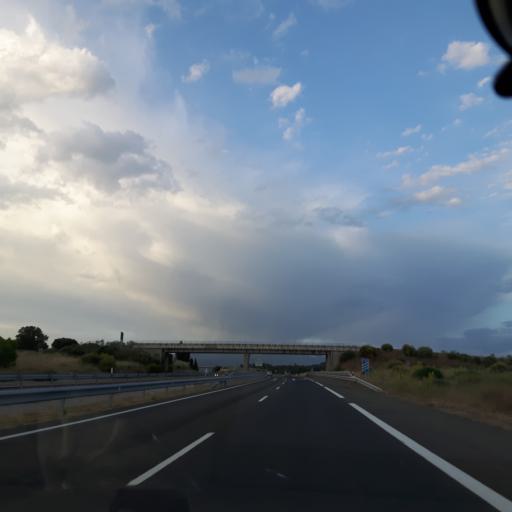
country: ES
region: Castille and Leon
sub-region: Provincia de Salamanca
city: Fuentes de Bejar
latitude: 40.5057
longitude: -5.6757
